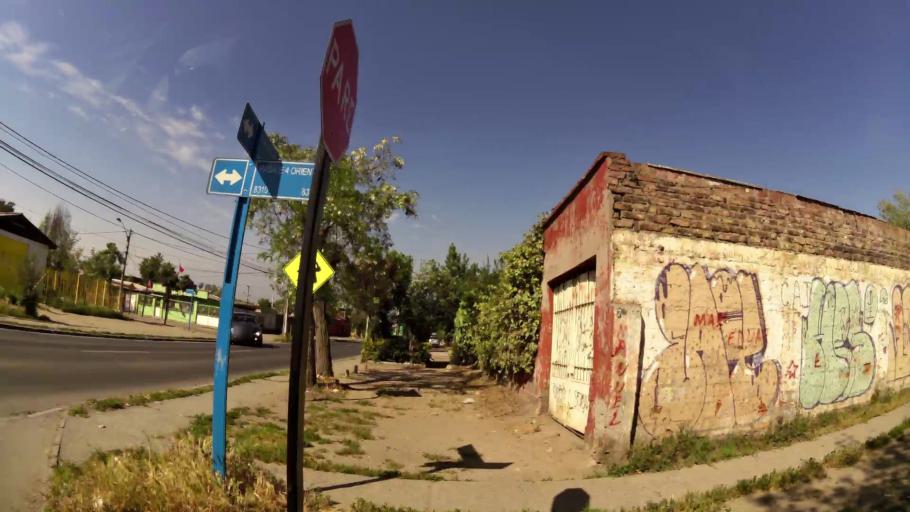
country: CL
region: Santiago Metropolitan
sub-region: Provincia de Santiago
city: La Pintana
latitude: -33.5377
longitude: -70.6176
